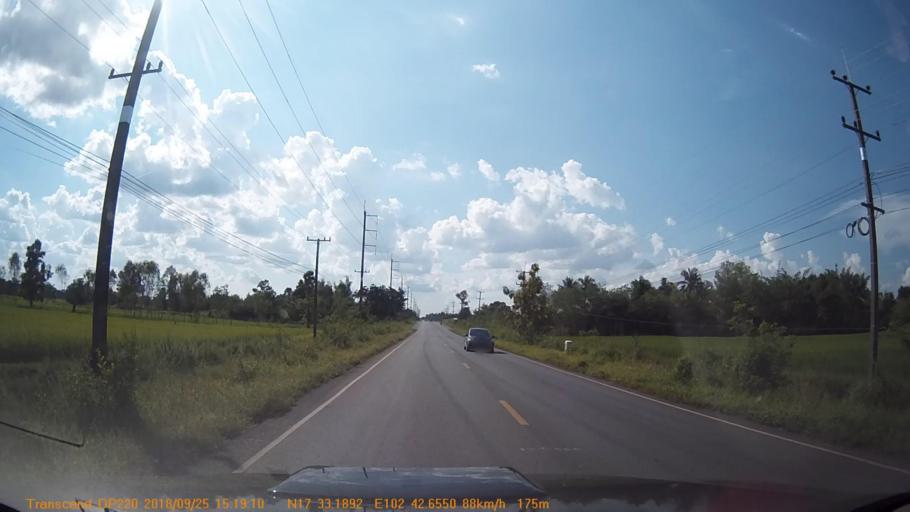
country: TH
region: Nong Khai
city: Sa Khrai
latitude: 17.5534
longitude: 102.7105
